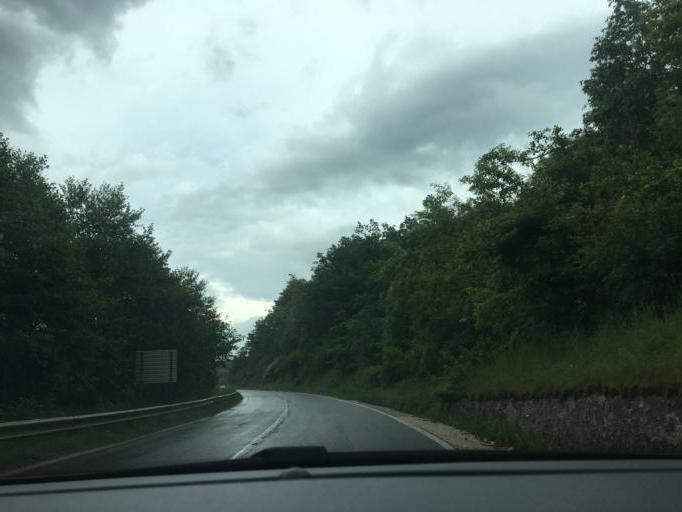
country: MK
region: Debarca
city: Belcista
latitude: 41.2827
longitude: 20.7884
